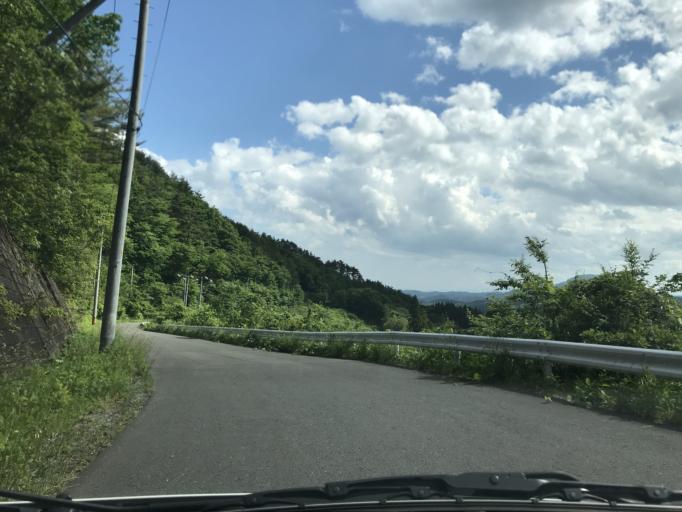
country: JP
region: Iwate
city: Ichinoseki
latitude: 38.8864
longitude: 140.9079
